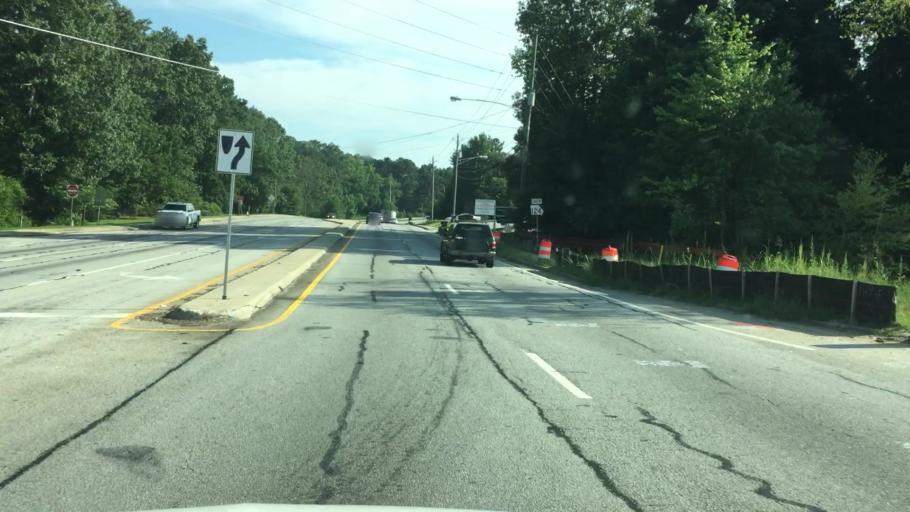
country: US
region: Georgia
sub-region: Gwinnett County
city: Snellville
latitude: 33.8529
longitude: -84.0229
